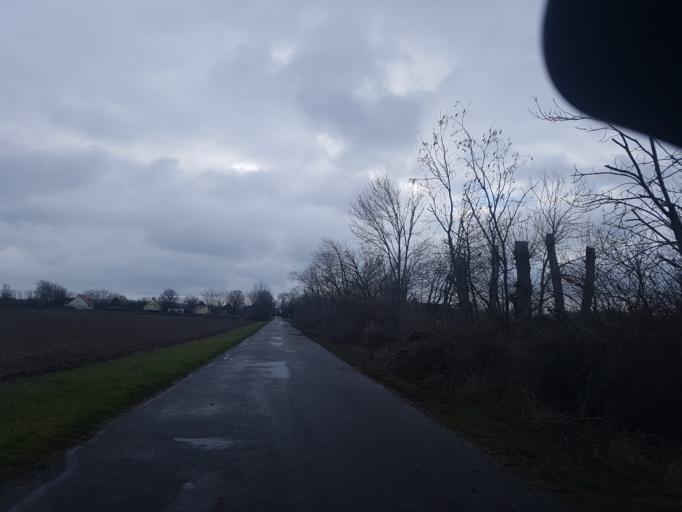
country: DE
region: Brandenburg
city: Muhlberg
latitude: 51.4096
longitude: 13.2239
